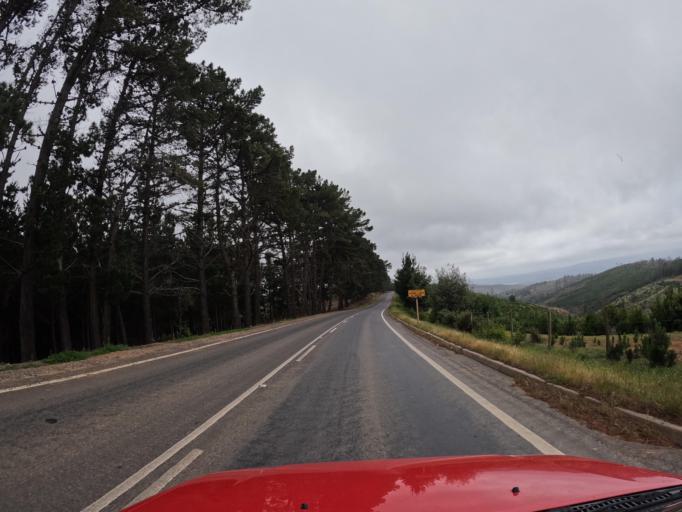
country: CL
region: O'Higgins
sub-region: Provincia de Colchagua
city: Santa Cruz
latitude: -34.5731
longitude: -72.0151
